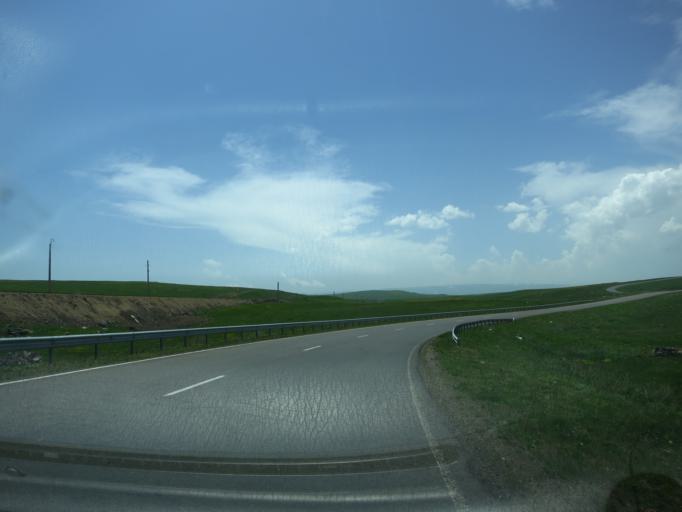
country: GE
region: Samtskhe-Javakheti
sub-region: Ninotsminda
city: Ninotsminda
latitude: 41.2930
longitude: 43.7349
